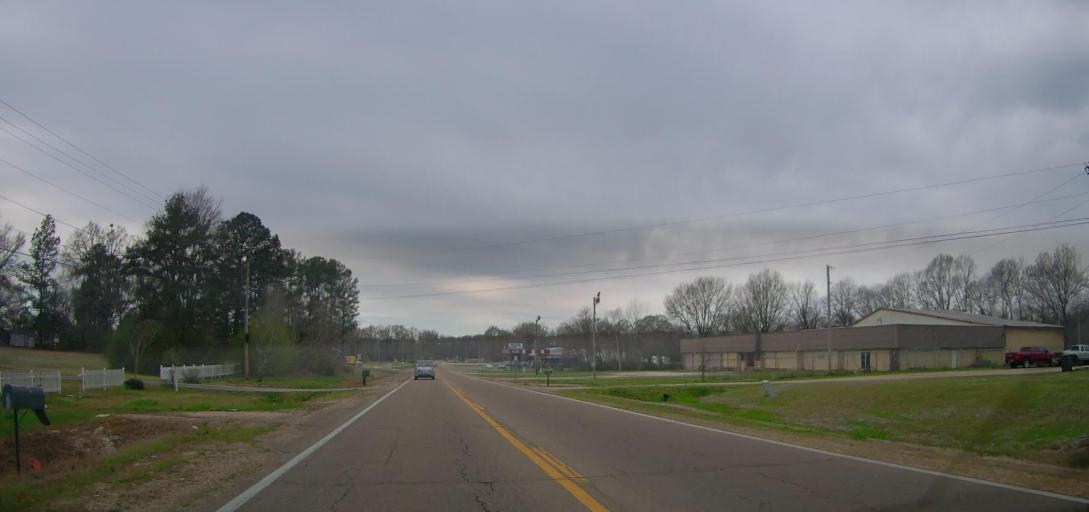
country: US
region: Mississippi
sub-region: Lee County
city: Plantersville
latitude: 34.2621
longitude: -88.6447
